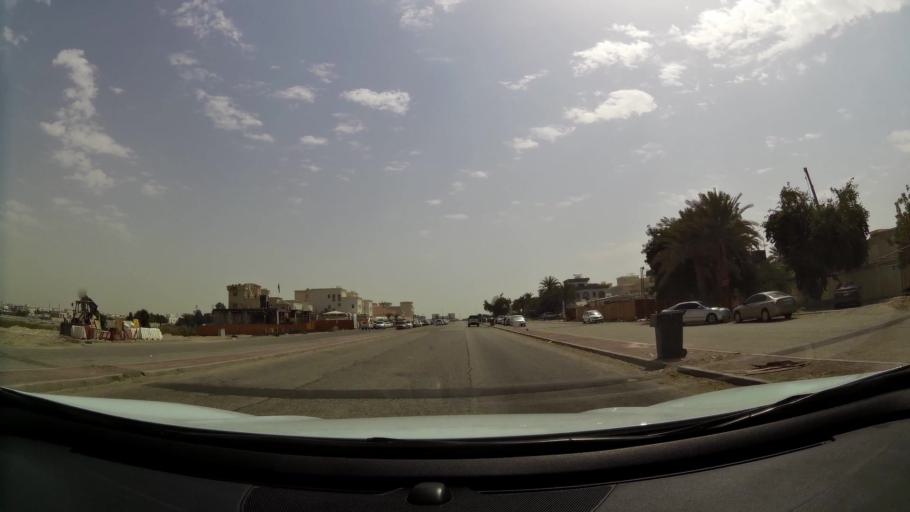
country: AE
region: Abu Dhabi
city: Abu Dhabi
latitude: 24.3013
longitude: 54.6281
